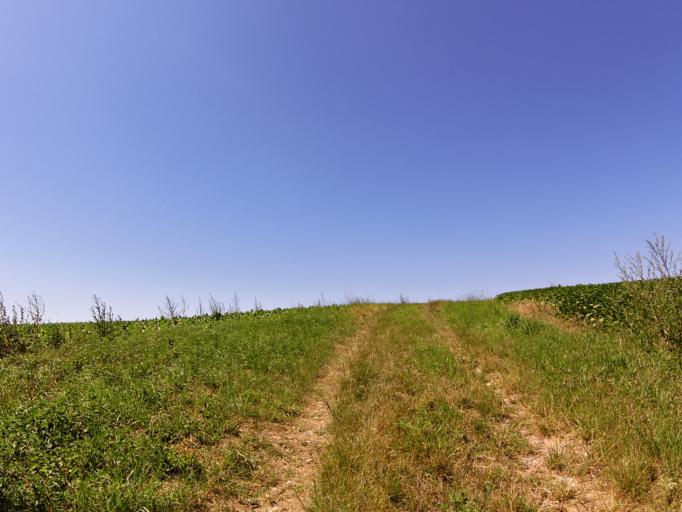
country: DE
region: Bavaria
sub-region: Regierungsbezirk Unterfranken
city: Gerbrunn
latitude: 49.7628
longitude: 10.0065
